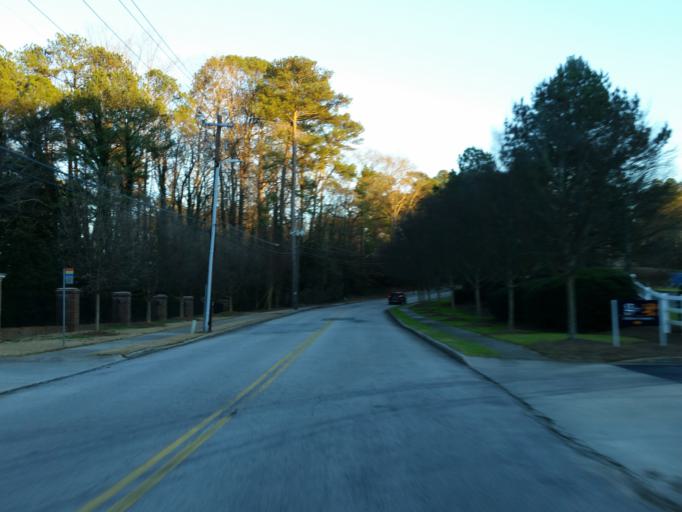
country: US
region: Georgia
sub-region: Cobb County
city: Vinings
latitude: 33.8215
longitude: -84.4381
